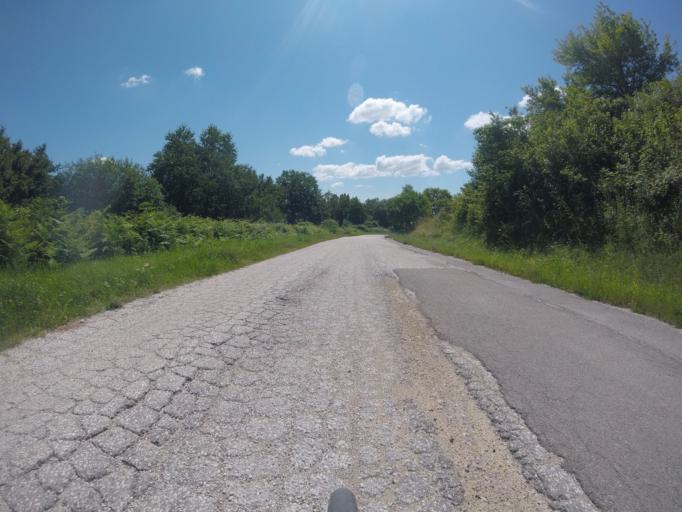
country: SI
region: Kostanjevica na Krki
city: Kostanjevica na Krki
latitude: 45.7754
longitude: 15.4686
